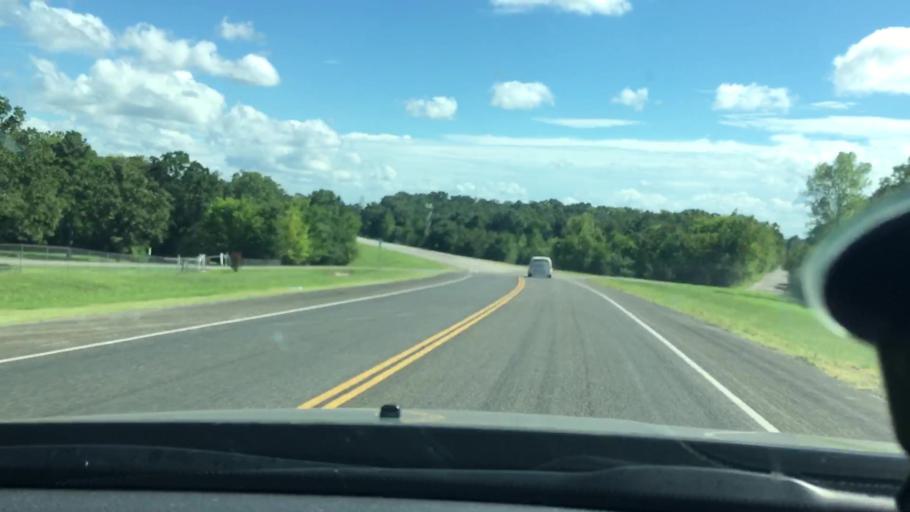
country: US
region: Oklahoma
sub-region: Sequoyah County
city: Vian
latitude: 35.5195
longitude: -94.9734
